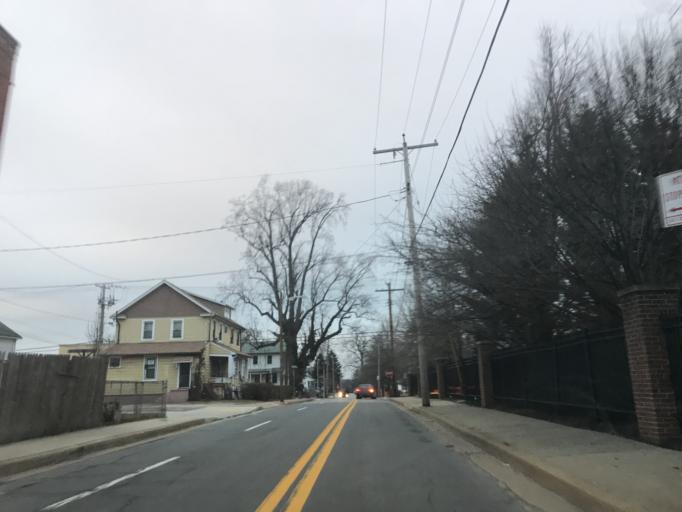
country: US
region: Maryland
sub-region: Baltimore County
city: Lochearn
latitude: 39.3535
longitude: -76.6782
